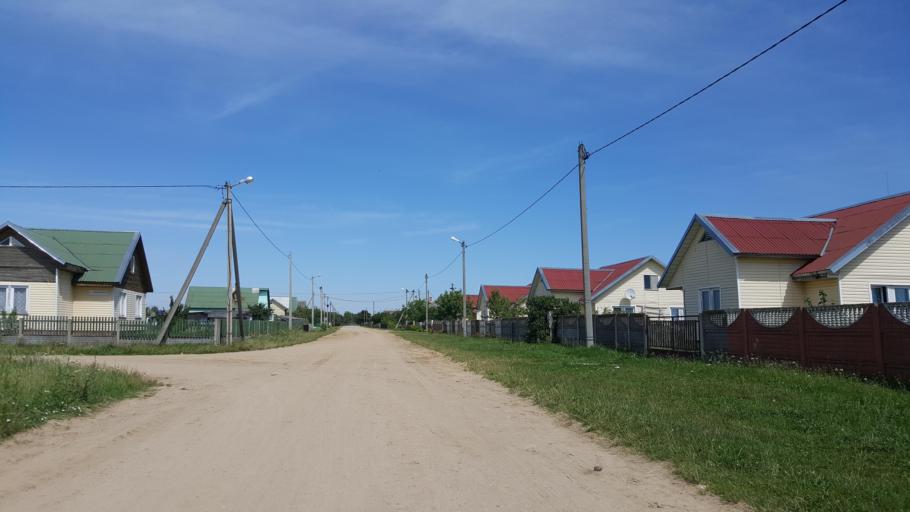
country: BY
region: Brest
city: Pruzhany
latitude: 52.5512
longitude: 24.2039
